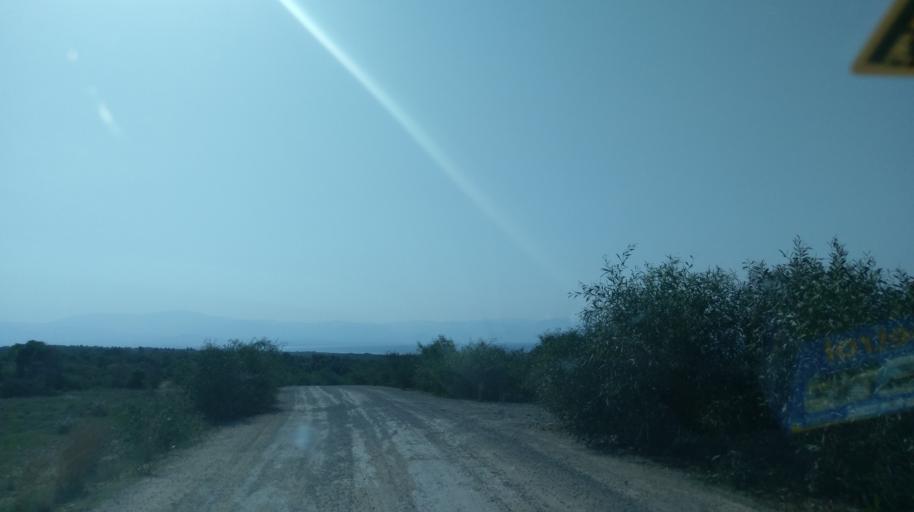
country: CY
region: Lefkosia
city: Morfou
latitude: 35.2839
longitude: 32.9442
